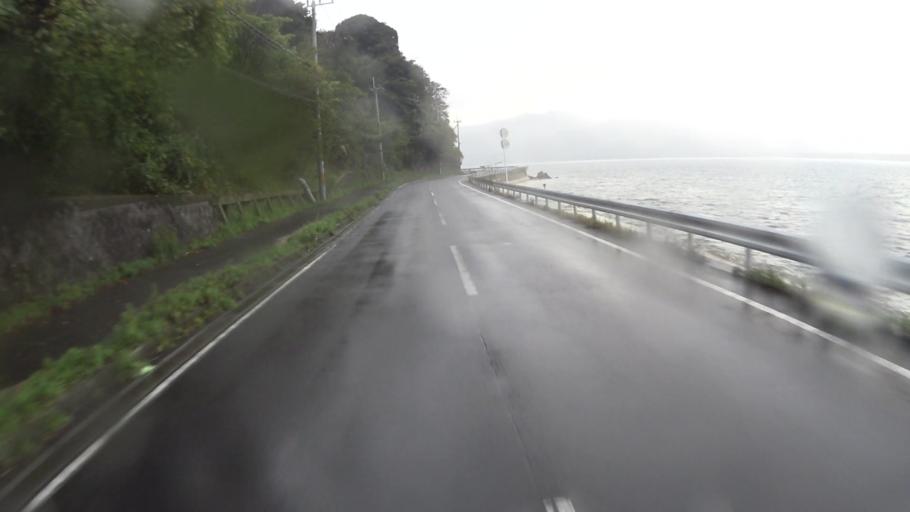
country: JP
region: Kyoto
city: Miyazu
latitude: 35.5619
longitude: 135.2066
